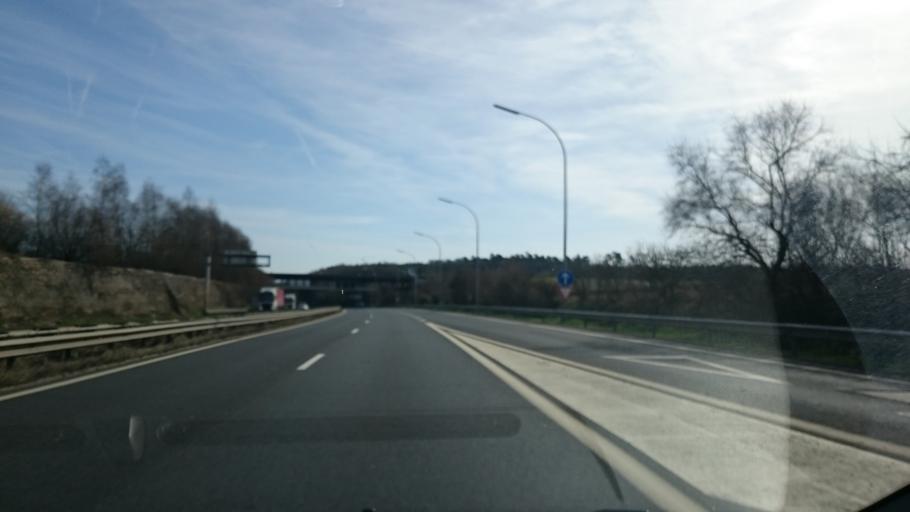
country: LU
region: Luxembourg
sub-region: Canton de Luxembourg
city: Niederanven
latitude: 49.6379
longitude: 6.2357
